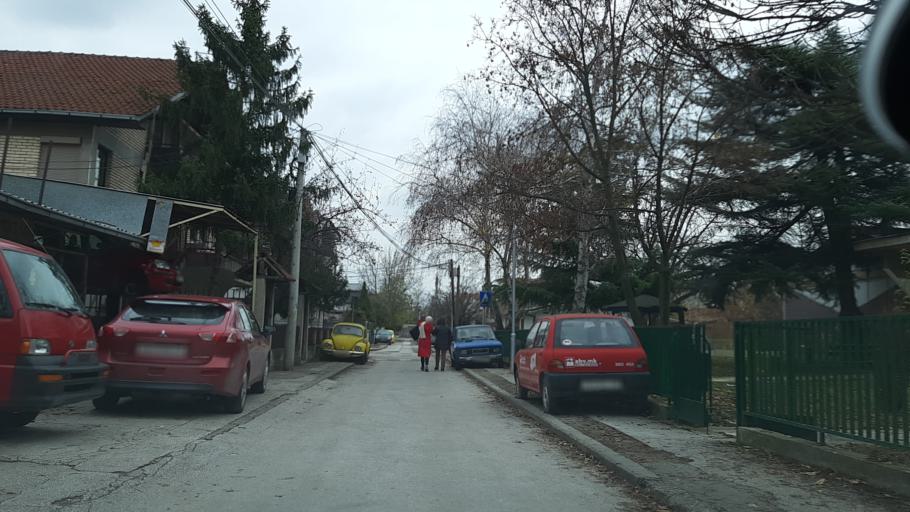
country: MK
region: Kisela Voda
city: Usje
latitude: 41.9772
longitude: 21.4667
